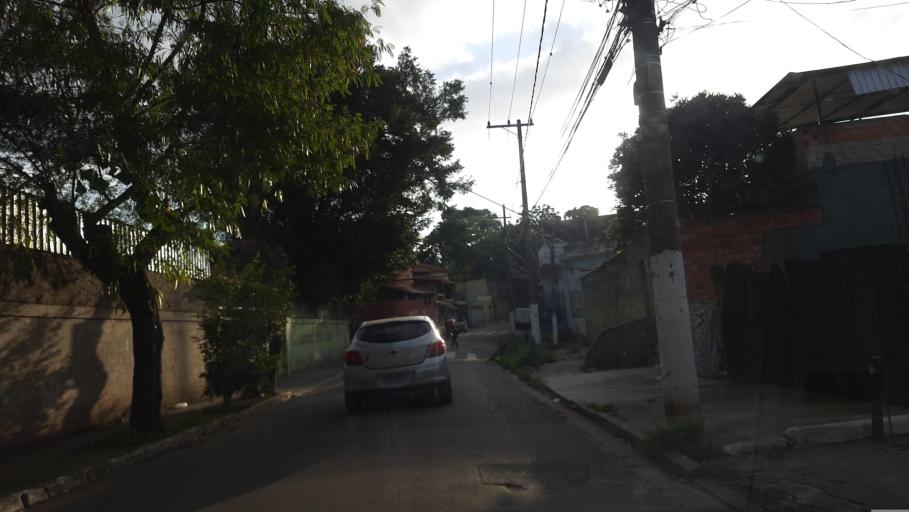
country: BR
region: Sao Paulo
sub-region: Caieiras
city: Caieiras
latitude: -23.4347
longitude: -46.7136
